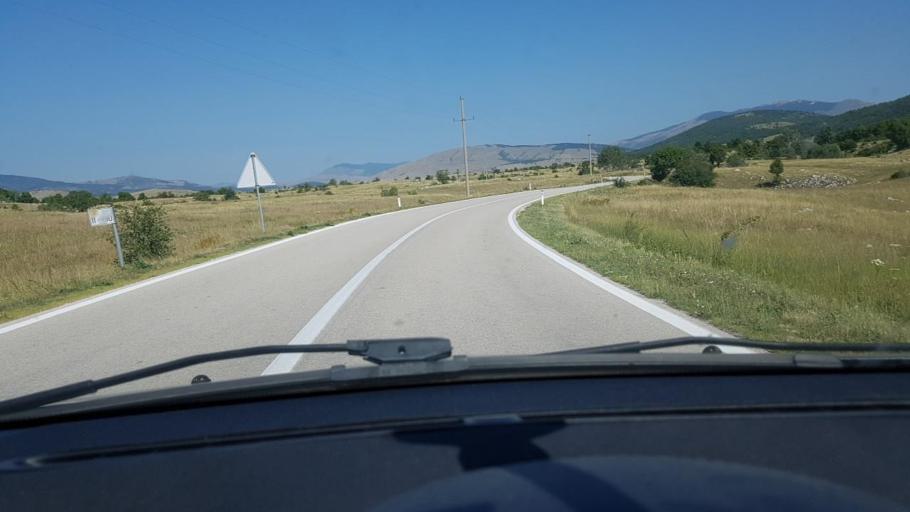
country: BA
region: Federation of Bosnia and Herzegovina
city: Bosansko Grahovo
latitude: 44.1371
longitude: 16.4746
